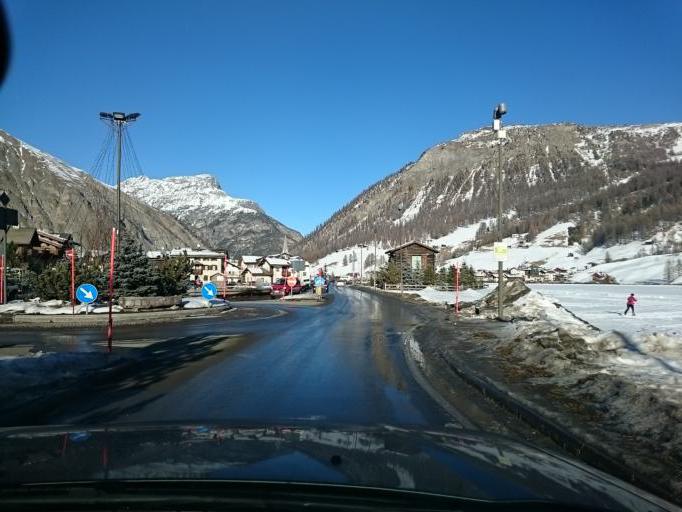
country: IT
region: Lombardy
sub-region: Provincia di Sondrio
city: Livigno
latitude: 46.5413
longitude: 10.1397
